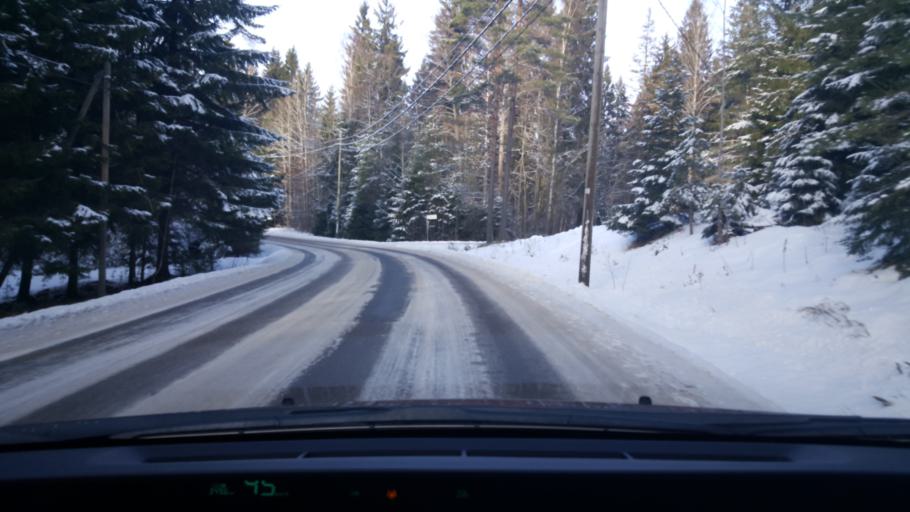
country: FI
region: Uusimaa
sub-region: Helsinki
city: Espoo
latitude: 60.3072
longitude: 24.5490
